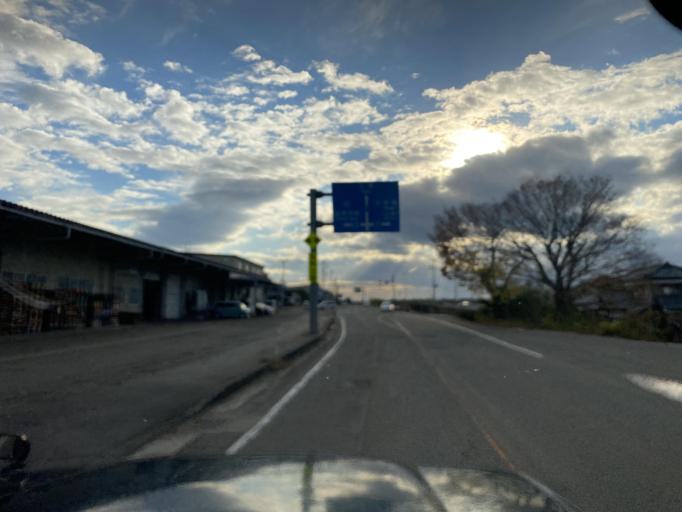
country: JP
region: Niigata
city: Kamo
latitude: 37.6804
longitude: 139.0188
